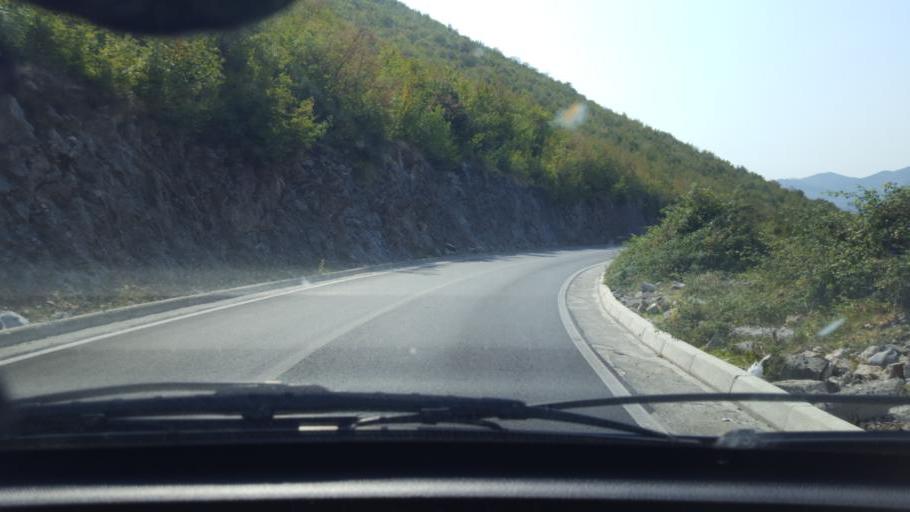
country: AL
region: Shkoder
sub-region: Rrethi i Malesia e Madhe
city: Kastrat
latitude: 42.3731
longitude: 19.4829
